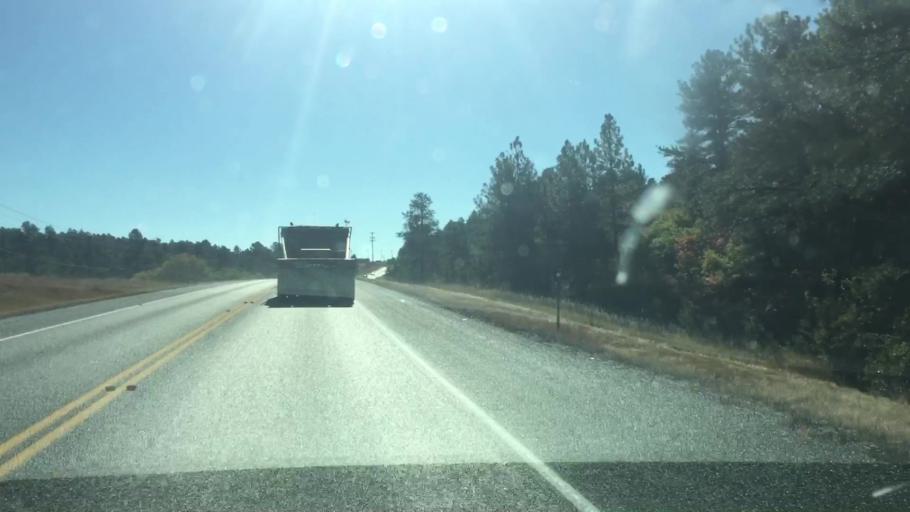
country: US
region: Colorado
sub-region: Elbert County
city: Ponderosa Park
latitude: 39.3743
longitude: -104.6875
